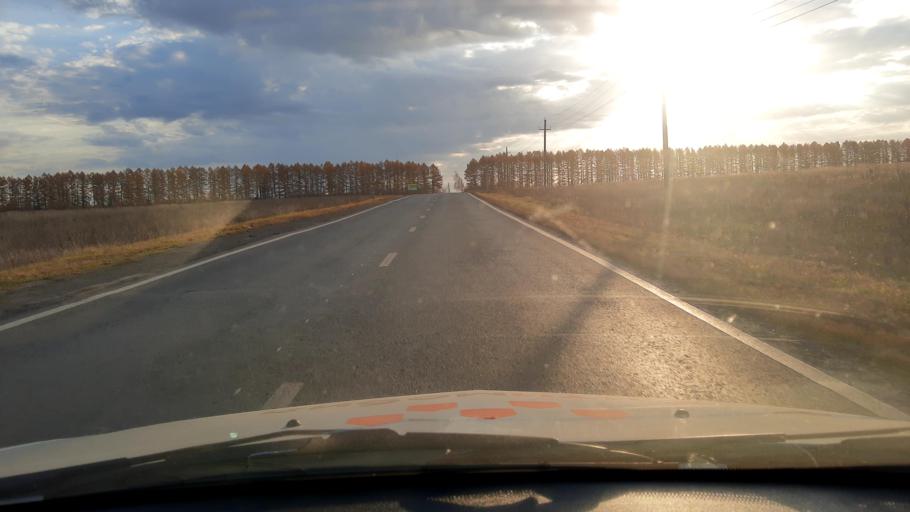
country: RU
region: Bashkortostan
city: Iglino
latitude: 54.7393
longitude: 56.2488
